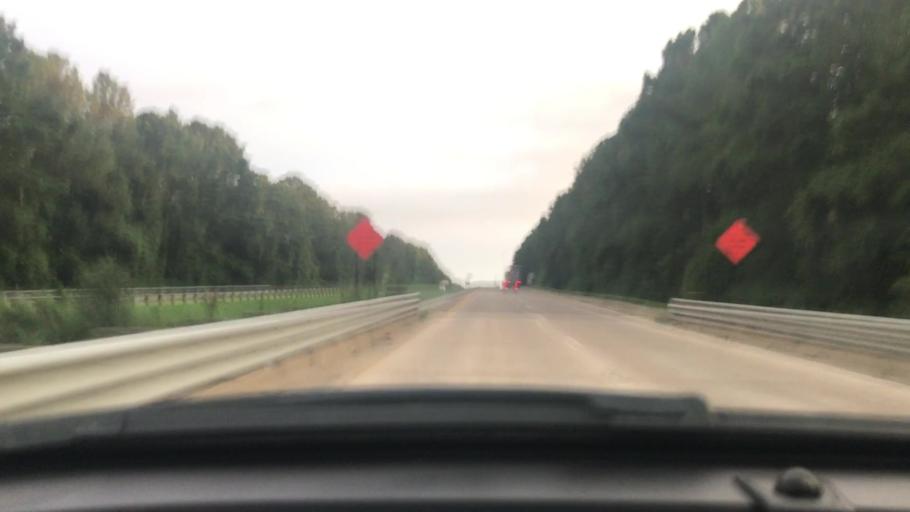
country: US
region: Louisiana
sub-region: Tangipahoa Parish
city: Kentwood
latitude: 30.9652
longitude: -90.5165
